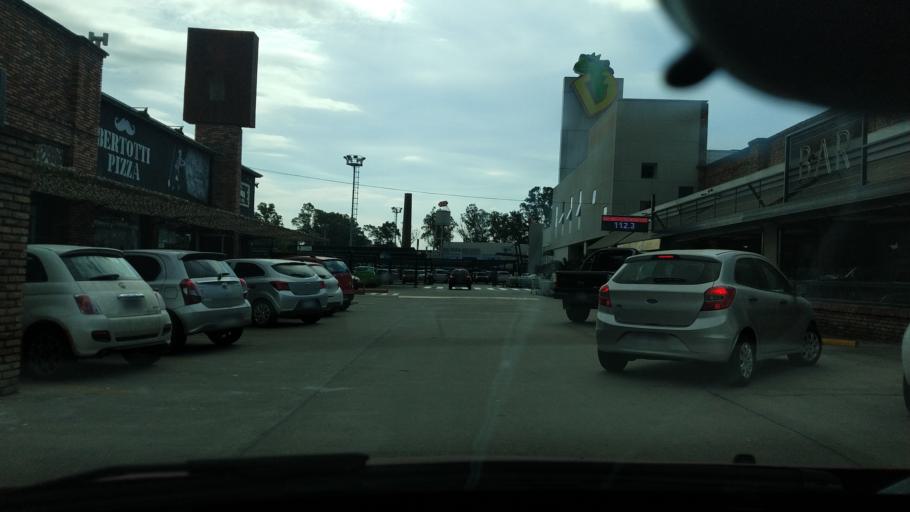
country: AR
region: Cordoba
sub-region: Departamento de Capital
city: Cordoba
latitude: -31.3679
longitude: -64.2197
